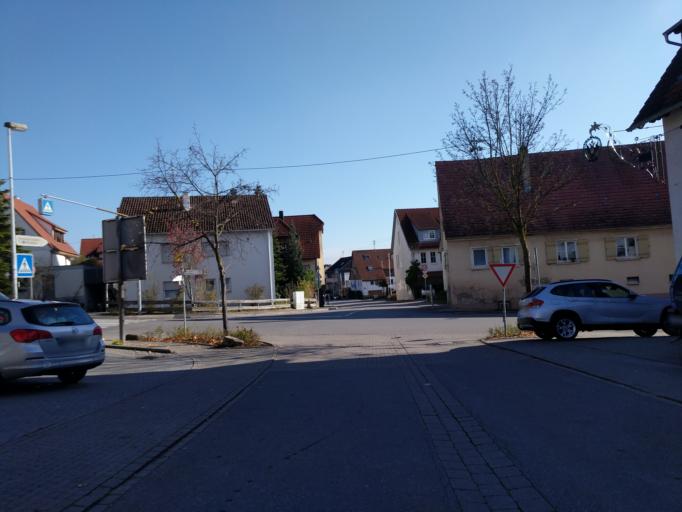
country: DE
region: Baden-Wuerttemberg
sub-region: Tuebingen Region
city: Rottenburg
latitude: 48.5031
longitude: 8.9623
